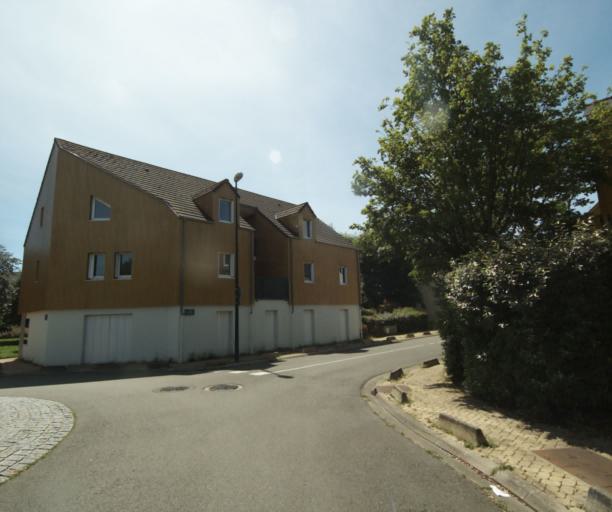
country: FR
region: Pays de la Loire
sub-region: Departement de la Mayenne
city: Change
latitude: 48.0789
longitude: -0.8051
